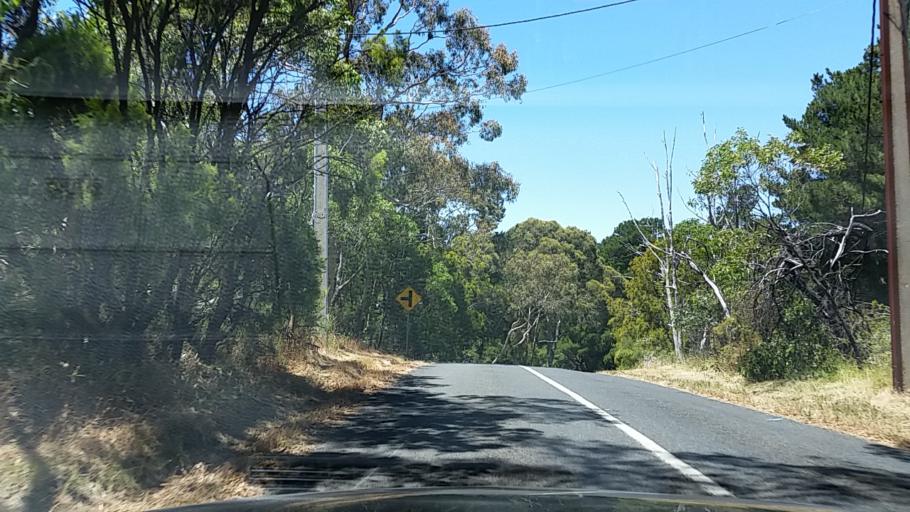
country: AU
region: South Australia
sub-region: Adelaide Hills
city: Crafers
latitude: -34.9997
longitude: 138.6869
